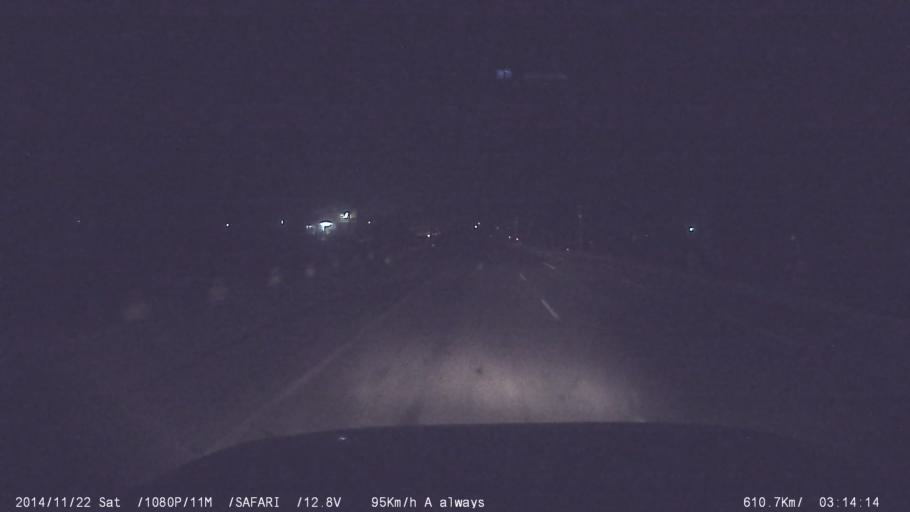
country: IN
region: Tamil Nadu
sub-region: Salem
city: Salem
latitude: 11.6093
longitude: 78.1006
